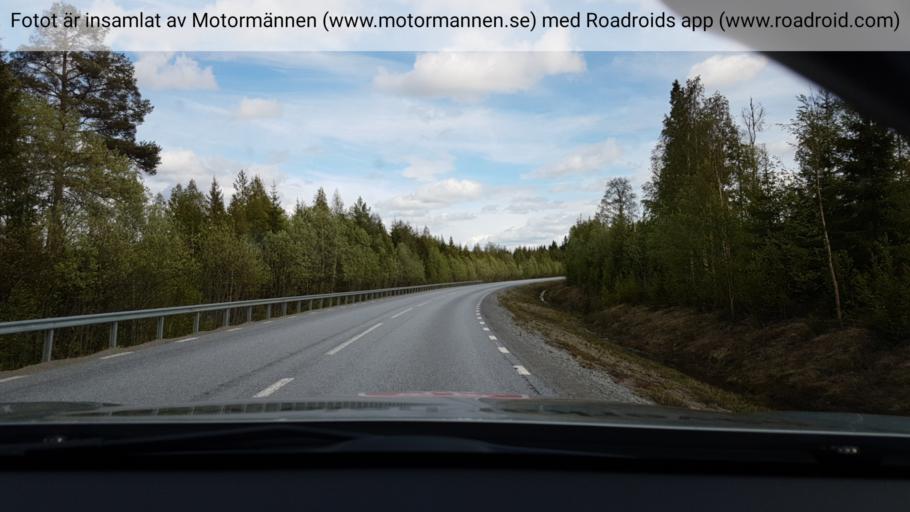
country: SE
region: Vaesterbotten
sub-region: Lycksele Kommun
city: Lycksele
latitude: 64.0536
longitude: 18.5511
